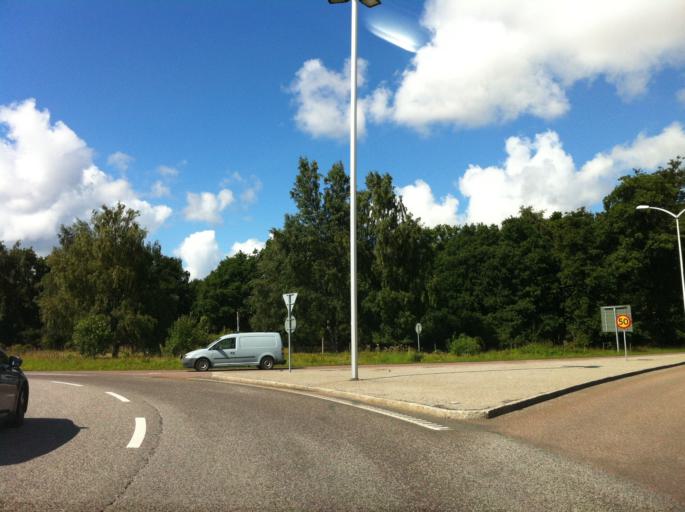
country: SE
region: Skane
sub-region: Bjuvs Kommun
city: Bjuv
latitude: 56.0818
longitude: 12.9244
